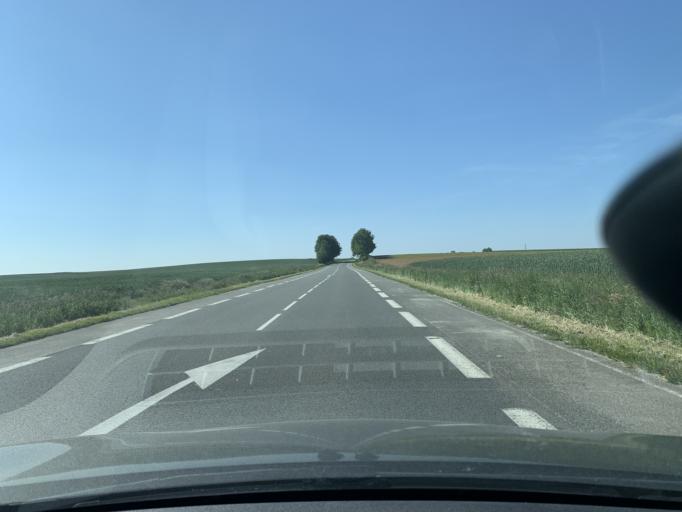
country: FR
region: Nord-Pas-de-Calais
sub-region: Departement du Nord
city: Rumilly-en-Cambresis
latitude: 50.1276
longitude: 3.2461
